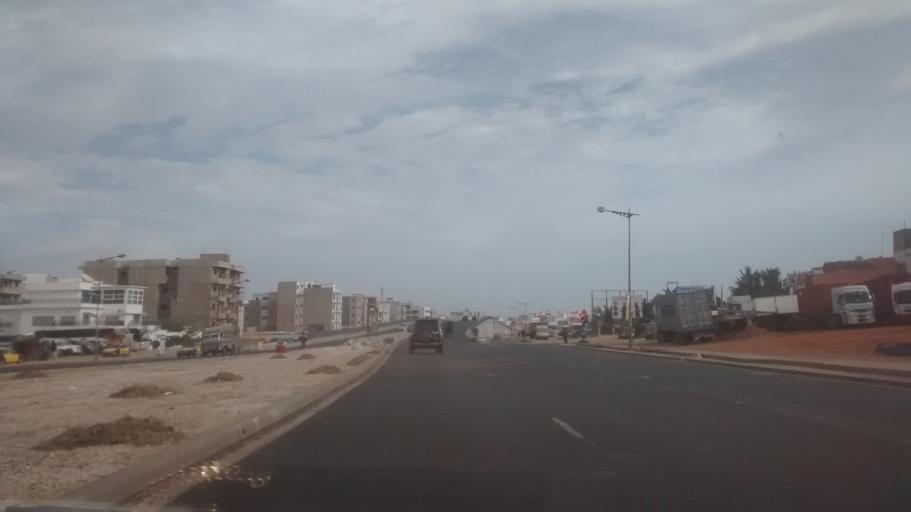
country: SN
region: Dakar
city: Grand Dakar
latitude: 14.7380
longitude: -17.4722
